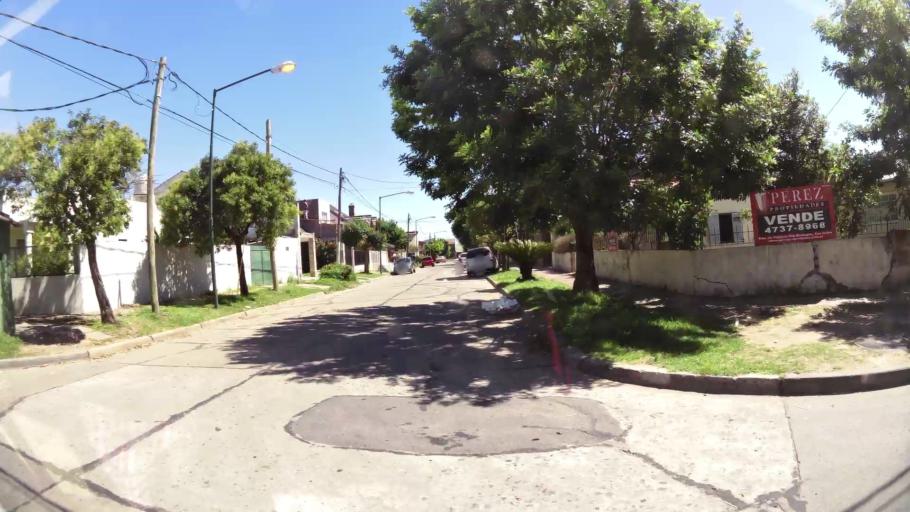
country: AR
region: Buenos Aires
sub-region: Partido de Tigre
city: Tigre
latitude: -34.5031
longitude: -58.5790
